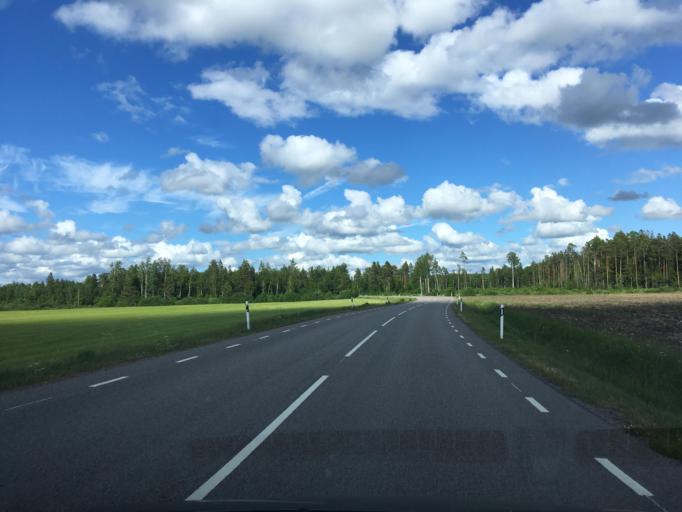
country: EE
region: Paernumaa
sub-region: Halinga vald
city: Parnu-Jaagupi
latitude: 58.6698
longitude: 24.5886
